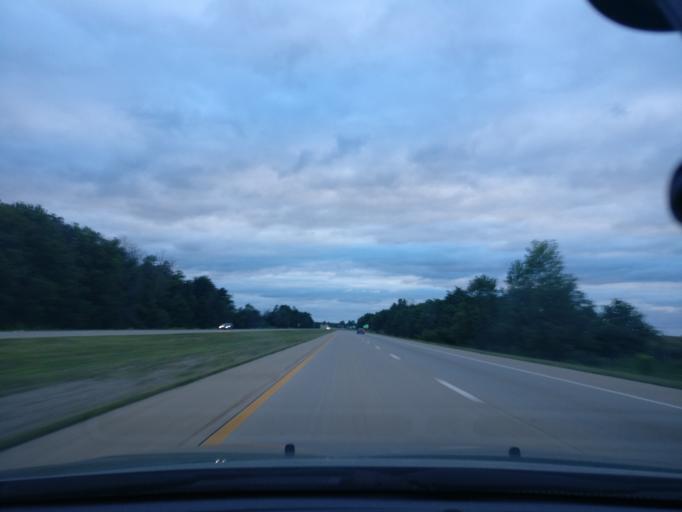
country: US
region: Ohio
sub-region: Greene County
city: Wilberforce
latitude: 39.6890
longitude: -83.8655
